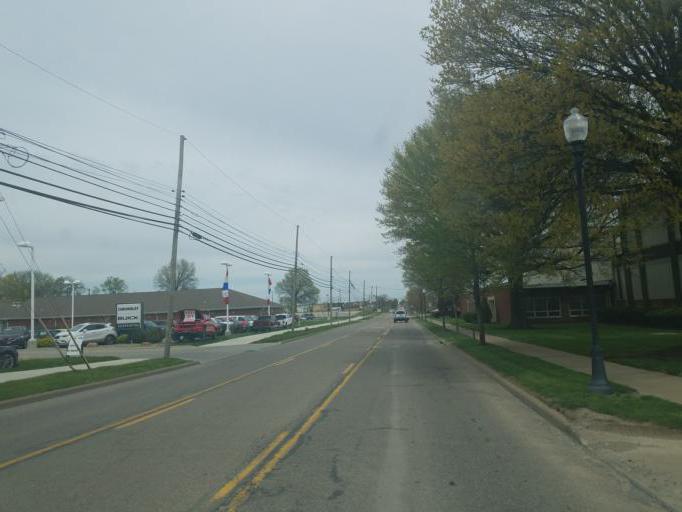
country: US
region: Ohio
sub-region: Wayne County
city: Orrville
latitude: 40.8511
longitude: -81.7639
